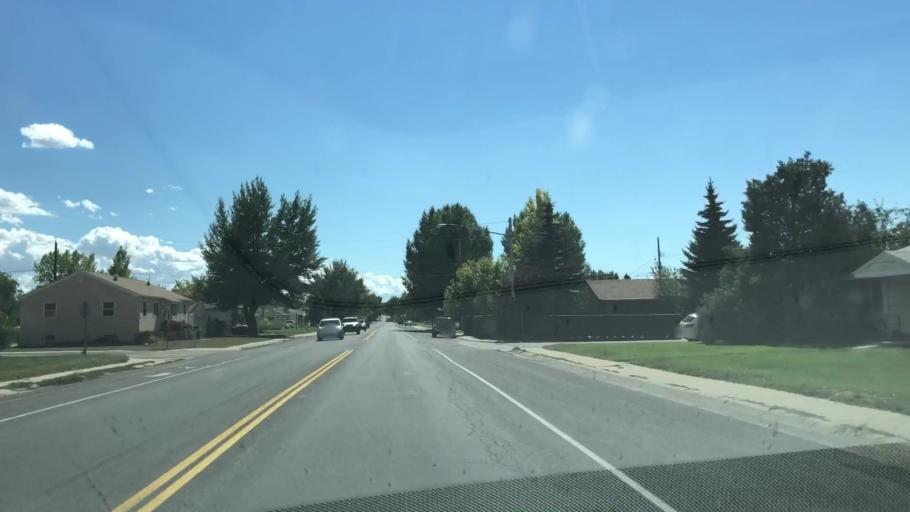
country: US
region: Wyoming
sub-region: Albany County
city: Laramie
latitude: 41.3250
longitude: -105.5842
